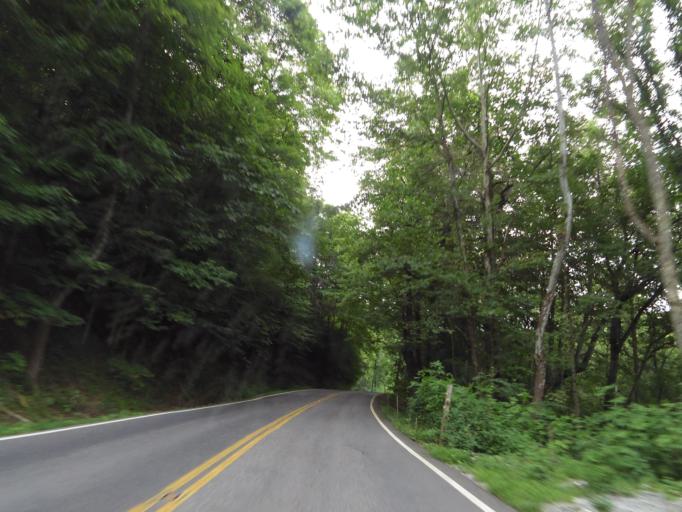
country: US
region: Tennessee
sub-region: Anderson County
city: Rocky Top
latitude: 36.1836
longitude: -84.1846
